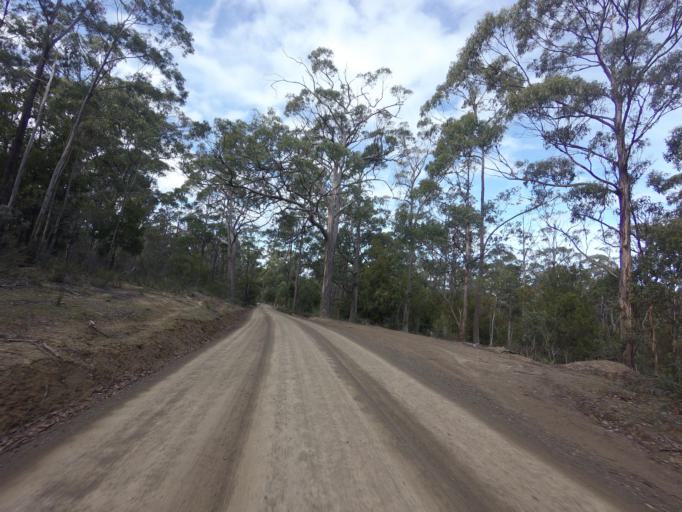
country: AU
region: Tasmania
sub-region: Clarence
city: Sandford
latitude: -43.0876
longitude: 147.7123
